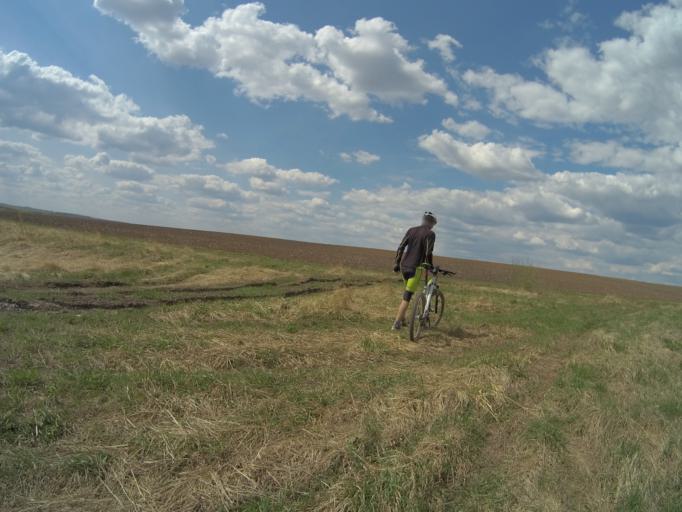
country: RU
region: Vladimir
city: Suzdal'
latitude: 56.3353
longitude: 40.3574
